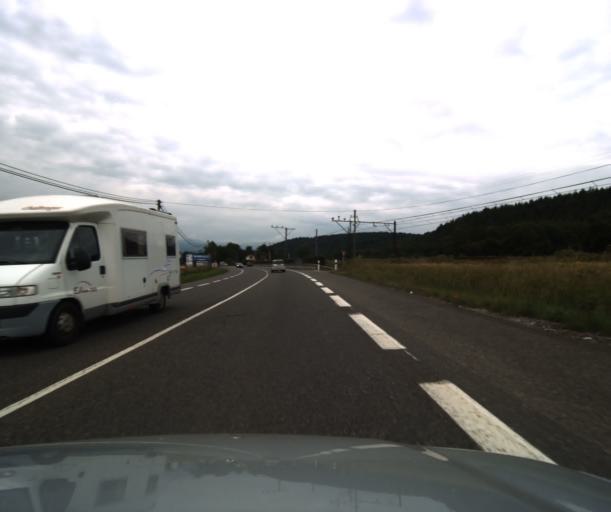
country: FR
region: Midi-Pyrenees
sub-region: Departement des Hautes-Pyrenees
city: Ossun
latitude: 43.1577
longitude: -0.0190
